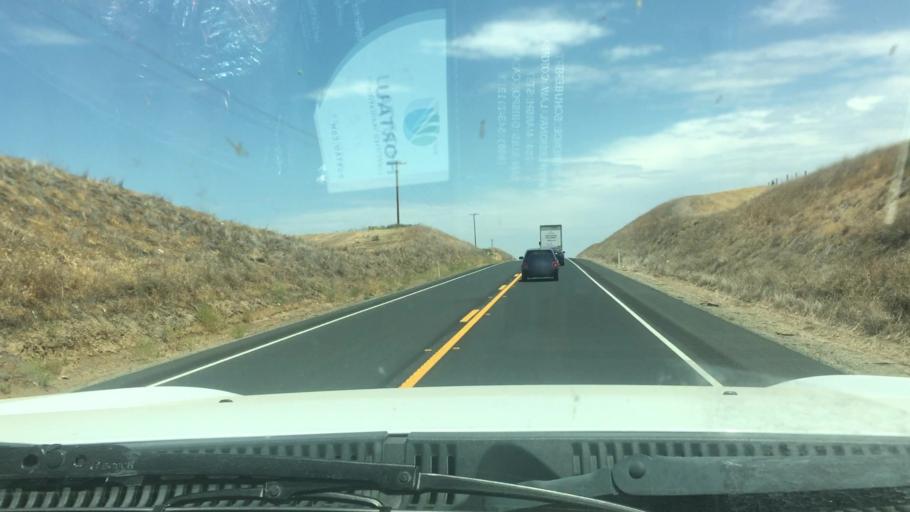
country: US
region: California
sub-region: Tulare County
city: Richgrove
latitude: 35.7713
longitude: -119.0533
